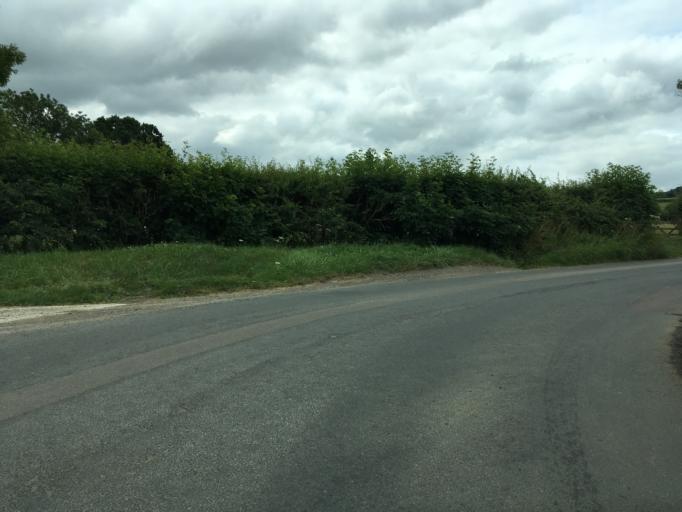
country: GB
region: England
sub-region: Oxfordshire
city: Shipton under Wychwood
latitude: 51.8858
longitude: -1.6490
